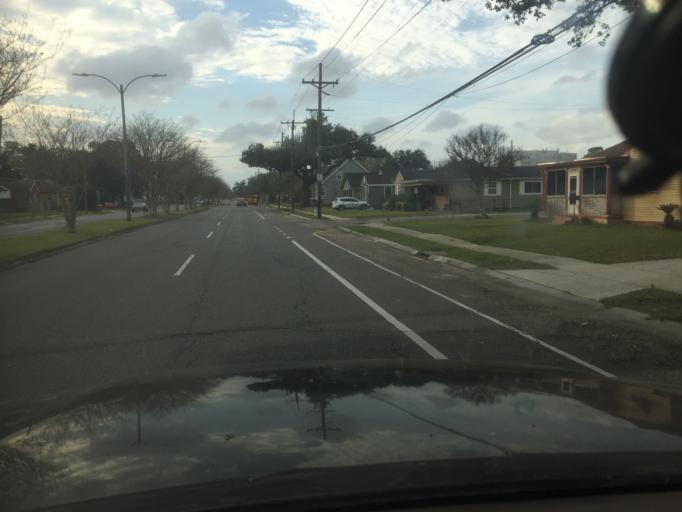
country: US
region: Louisiana
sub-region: Orleans Parish
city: New Orleans
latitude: 29.9888
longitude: -90.0789
